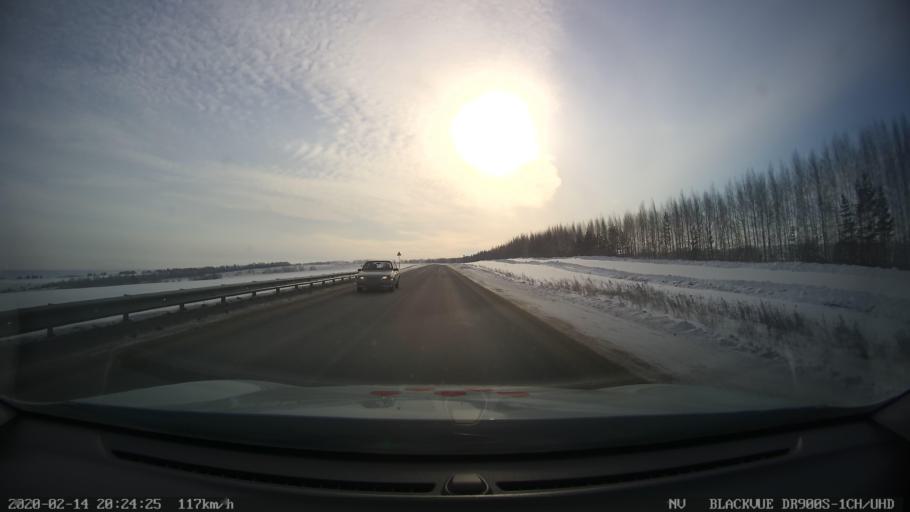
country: RU
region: Tatarstan
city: Verkhniy Uslon
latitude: 55.5125
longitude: 48.9697
